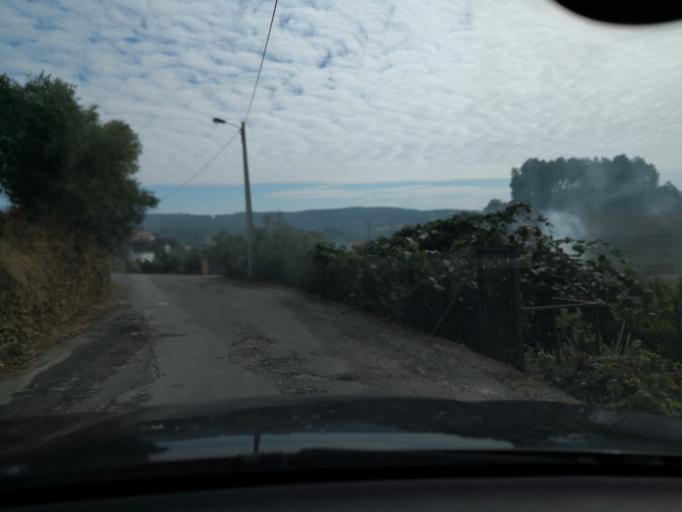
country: PT
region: Vila Real
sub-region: Sabrosa
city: Vilela
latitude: 41.2230
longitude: -7.6925
